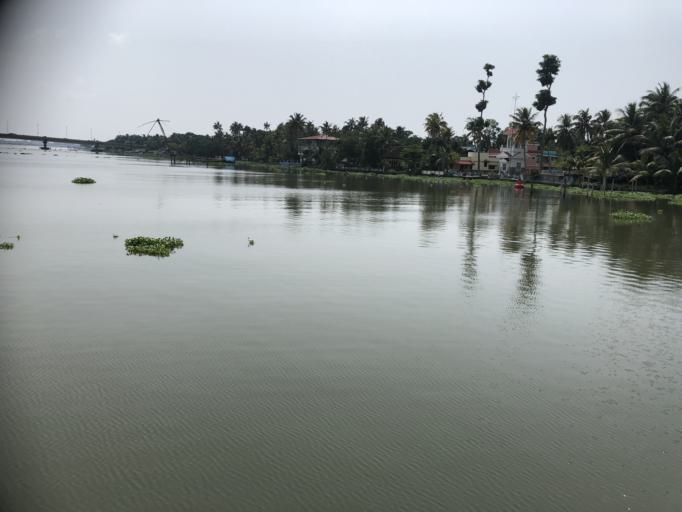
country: IN
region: Kerala
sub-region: Ernakulam
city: Cochin
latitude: 9.9964
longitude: 76.2658
